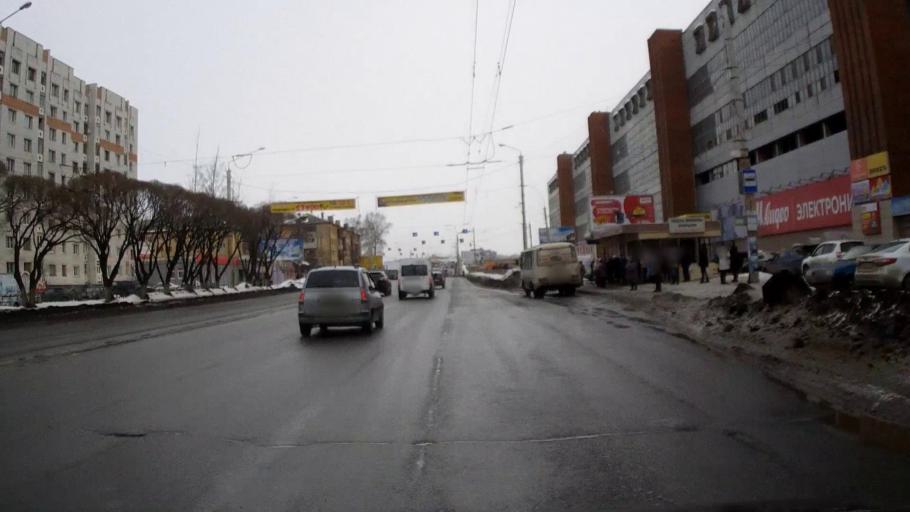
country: RU
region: Vologda
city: Vologda
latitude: 59.2125
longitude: 39.8536
